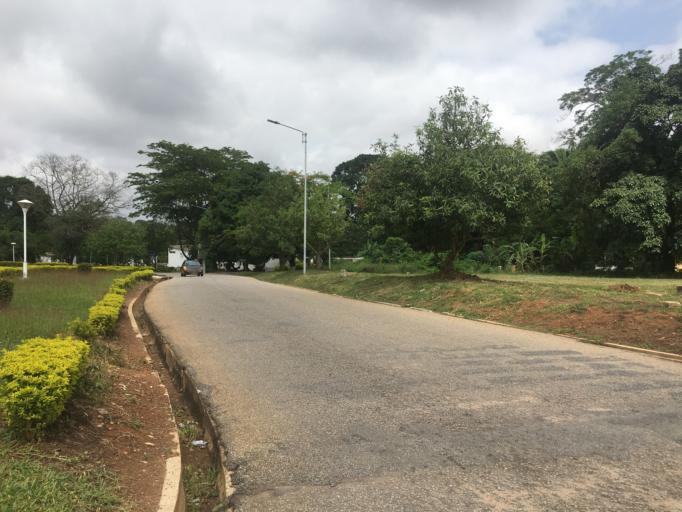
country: GH
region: Ashanti
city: Kumasi
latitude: 6.6800
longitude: -1.5736
